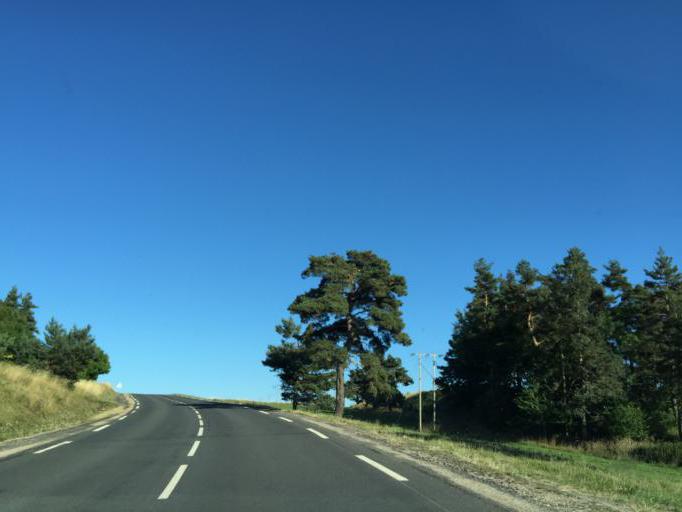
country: FR
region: Auvergne
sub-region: Departement de la Haute-Loire
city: Bains
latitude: 44.9850
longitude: 3.7117
